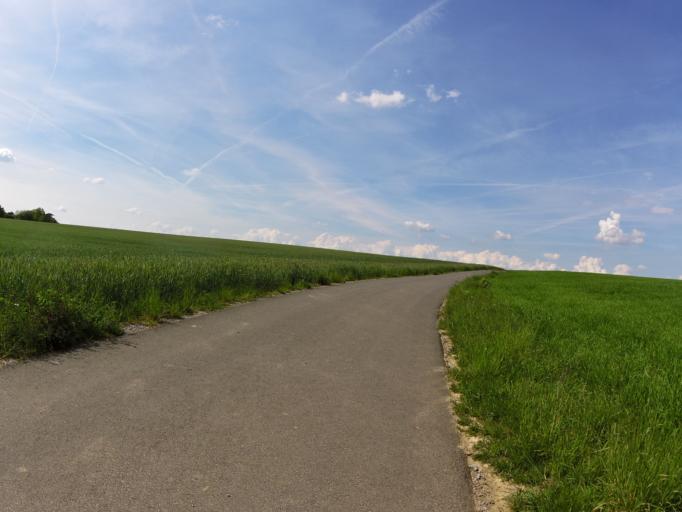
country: DE
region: Bavaria
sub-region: Regierungsbezirk Unterfranken
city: Theilheim
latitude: 49.7363
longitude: 10.0252
